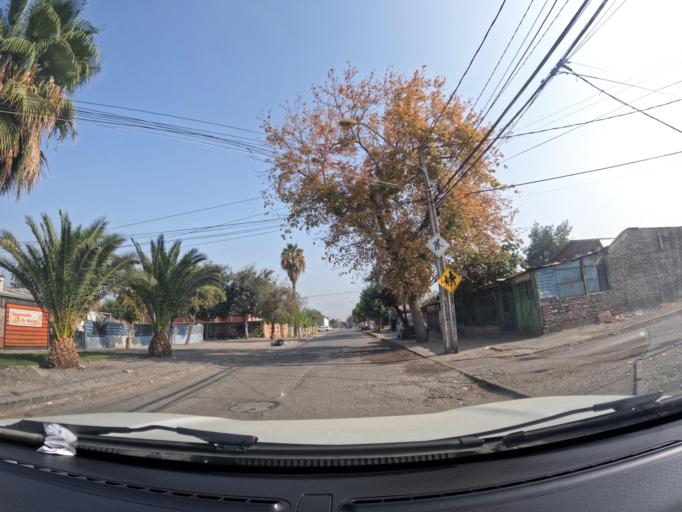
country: CL
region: Santiago Metropolitan
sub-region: Provincia de Santiago
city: Villa Presidente Frei, Nunoa, Santiago, Chile
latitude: -33.4737
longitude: -70.5689
